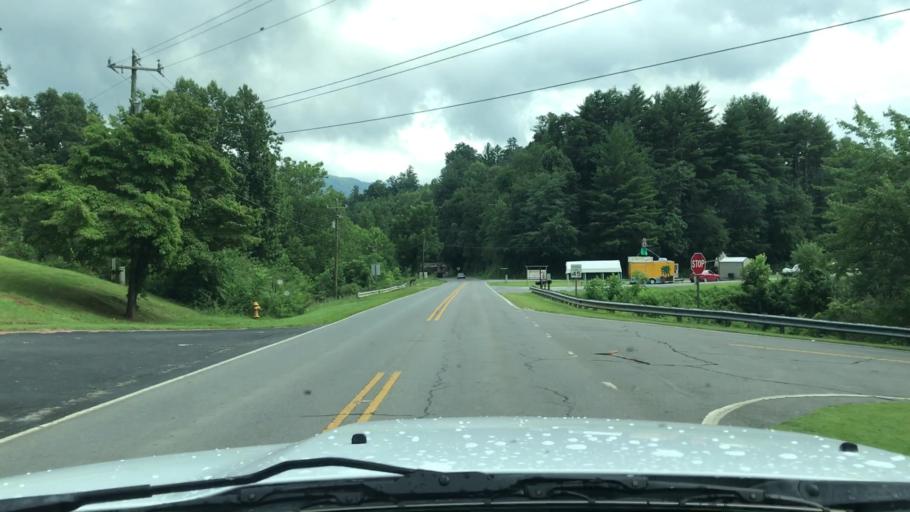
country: US
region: North Carolina
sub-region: Graham County
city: Robbinsville
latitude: 35.3338
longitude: -83.8128
